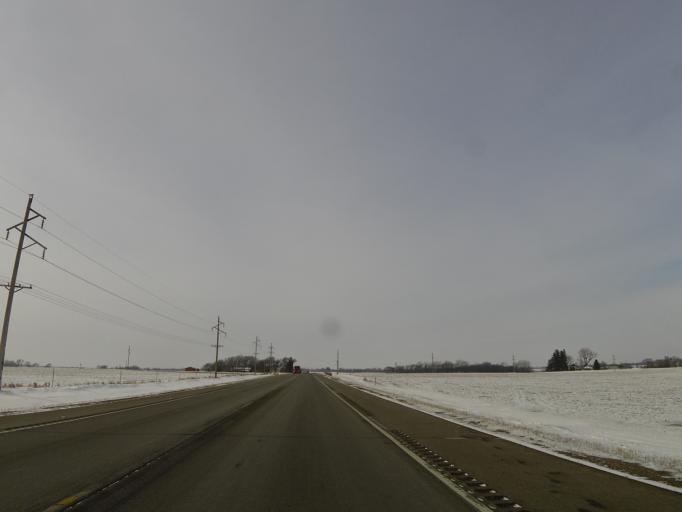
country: US
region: Minnesota
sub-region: Carver County
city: Mayer
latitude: 44.9061
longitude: -93.9464
